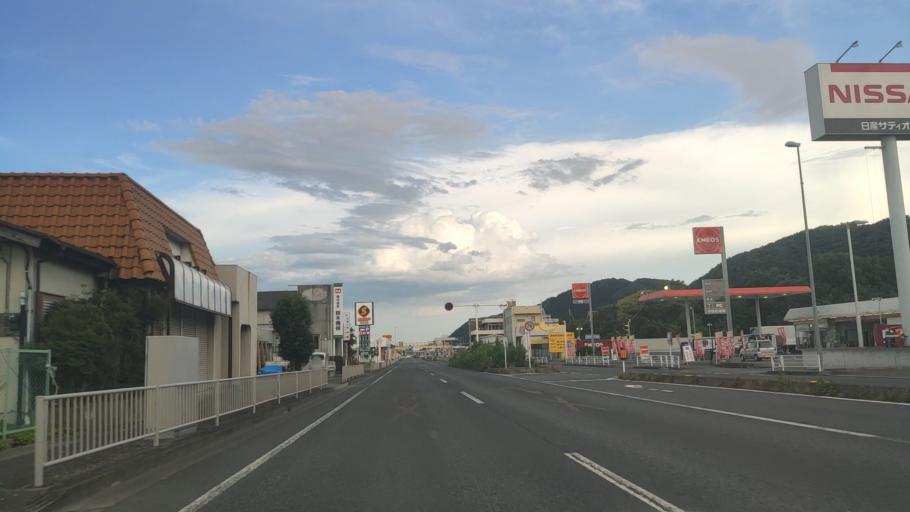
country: JP
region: Gunma
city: Kiryu
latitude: 36.3789
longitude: 139.3440
